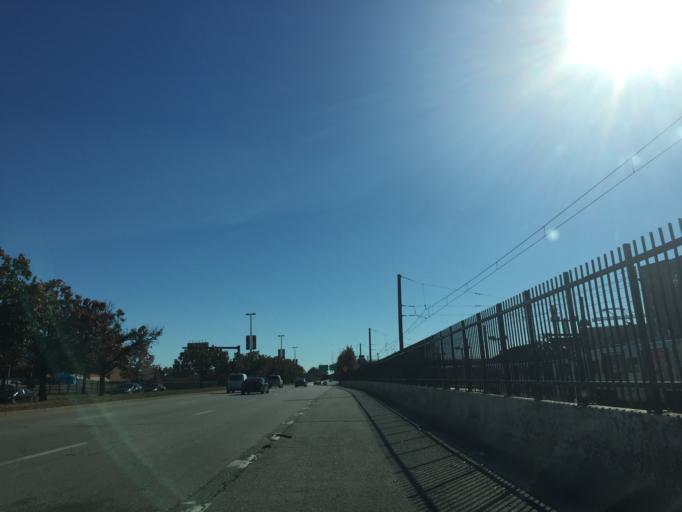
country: US
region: Maryland
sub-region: City of Baltimore
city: Baltimore
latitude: 39.2837
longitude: -76.6191
